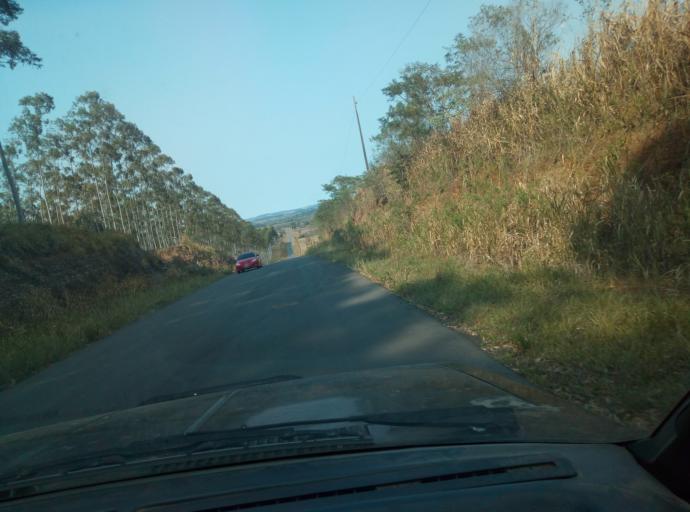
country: PY
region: Caaguazu
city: Carayao
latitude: -25.2502
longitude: -56.2880
